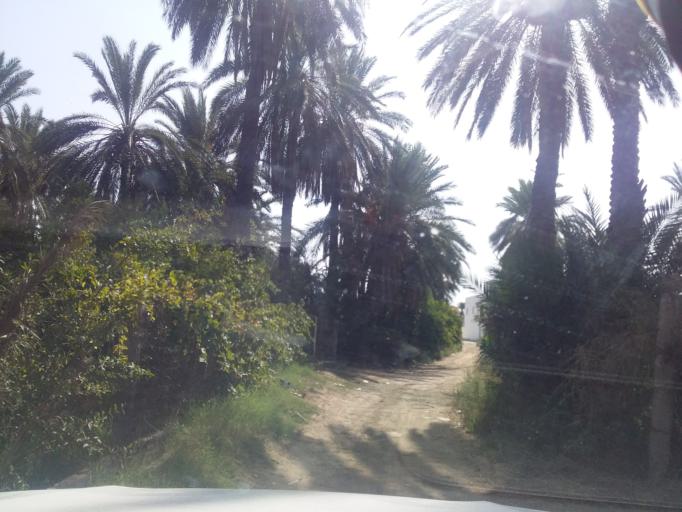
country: TN
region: Qabis
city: Gabes
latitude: 33.6242
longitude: 10.2872
